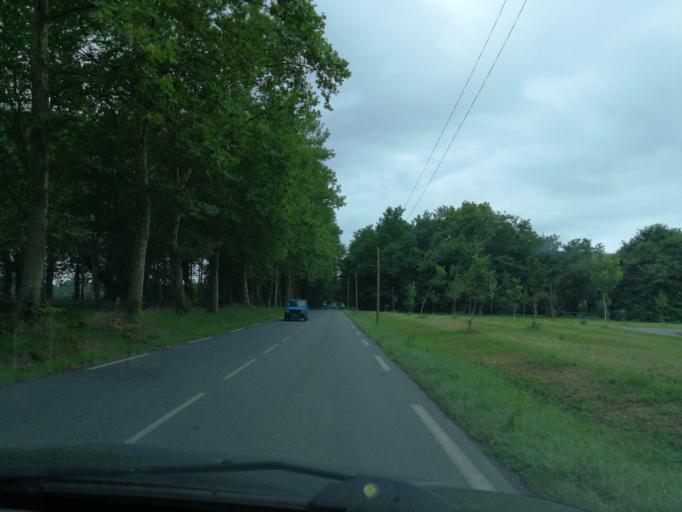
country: FR
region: Midi-Pyrenees
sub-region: Departement des Hautes-Pyrenees
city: Bazet
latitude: 43.2758
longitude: 0.0820
